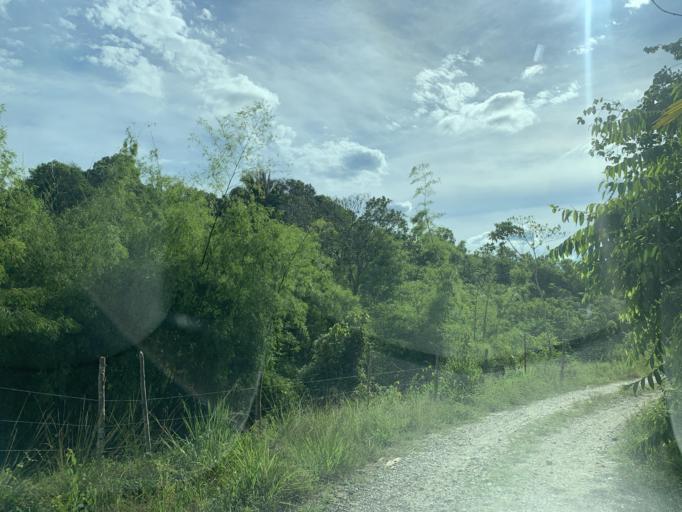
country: CO
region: Boyaca
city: Puerto Boyaca
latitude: 6.0097
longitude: -74.3846
